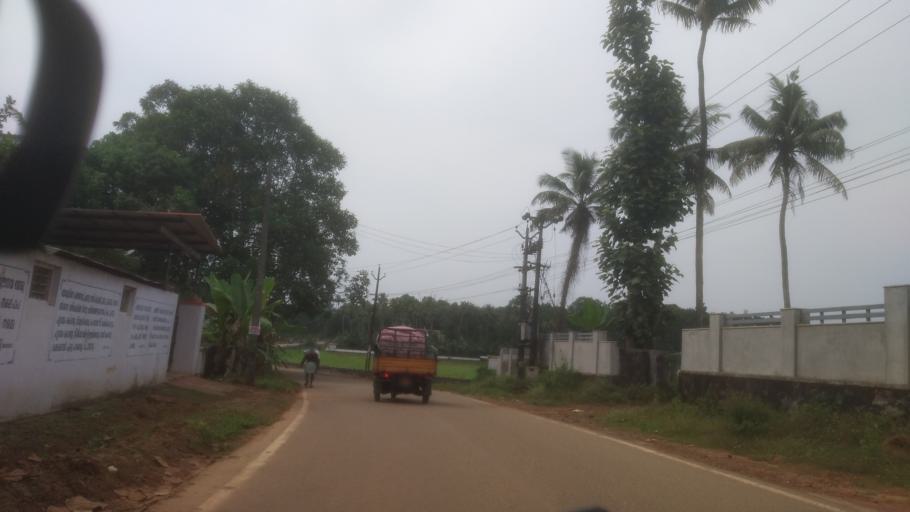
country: IN
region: Kerala
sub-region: Ernakulam
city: Muvattupula
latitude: 10.0476
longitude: 76.5302
